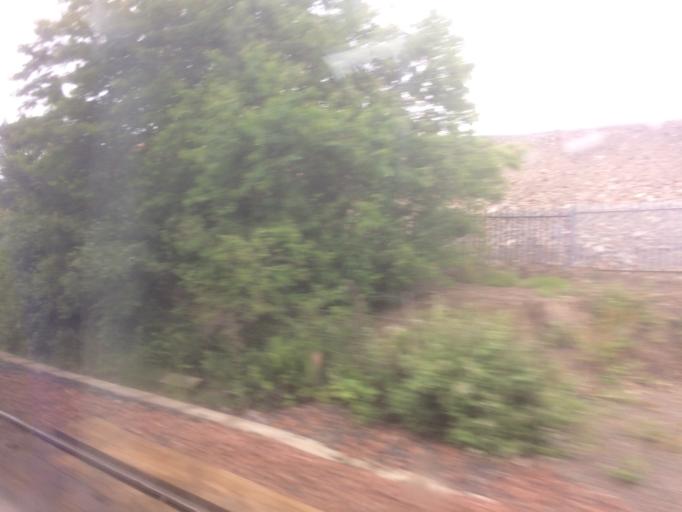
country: GB
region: Scotland
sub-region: Glasgow City
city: Glasgow
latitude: 55.8767
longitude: -4.2419
